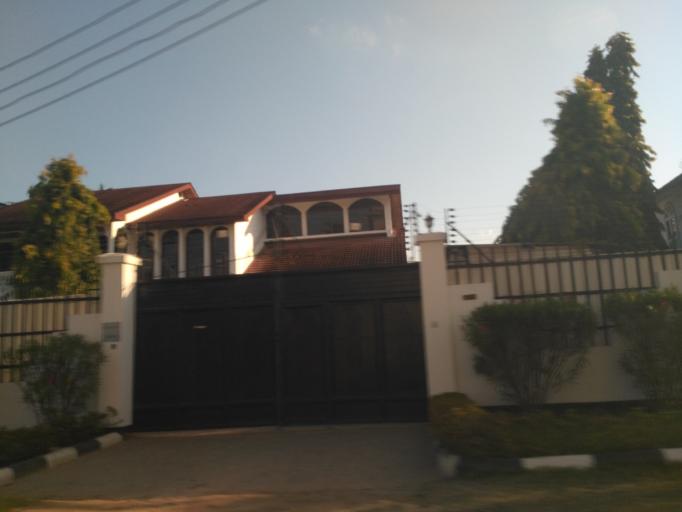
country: TZ
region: Dar es Salaam
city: Magomeni
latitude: -6.7603
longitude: 39.2550
